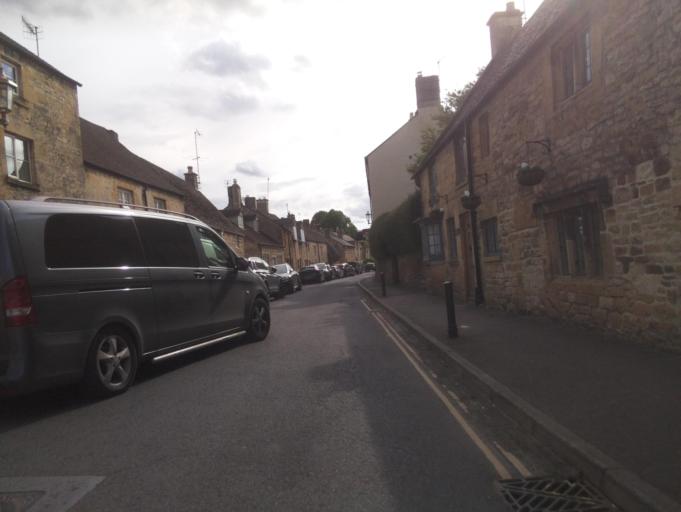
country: GB
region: England
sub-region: Gloucestershire
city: Chipping Campden
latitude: 52.0491
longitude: -1.7855
